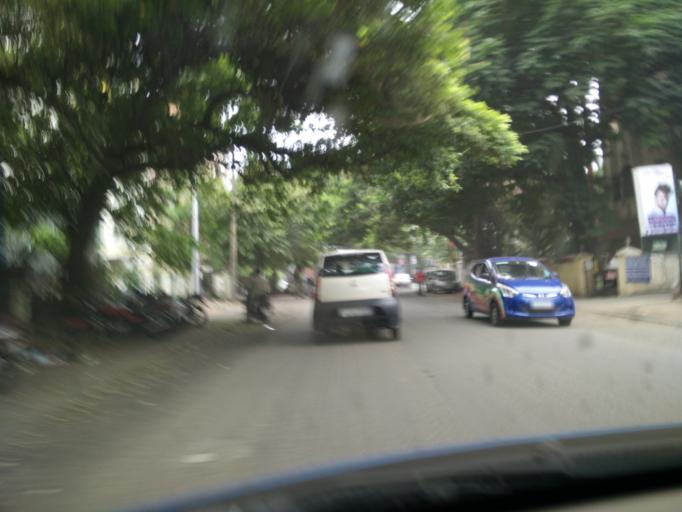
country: IN
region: Tamil Nadu
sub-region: Chennai
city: Gandhi Nagar
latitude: 12.9989
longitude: 80.2516
